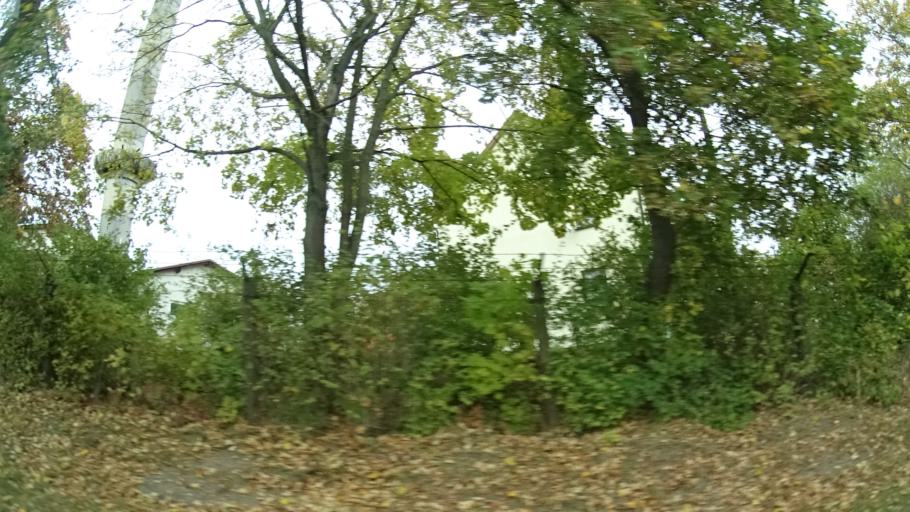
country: DE
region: Thuringia
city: Rippershausen
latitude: 50.6016
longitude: 10.3683
